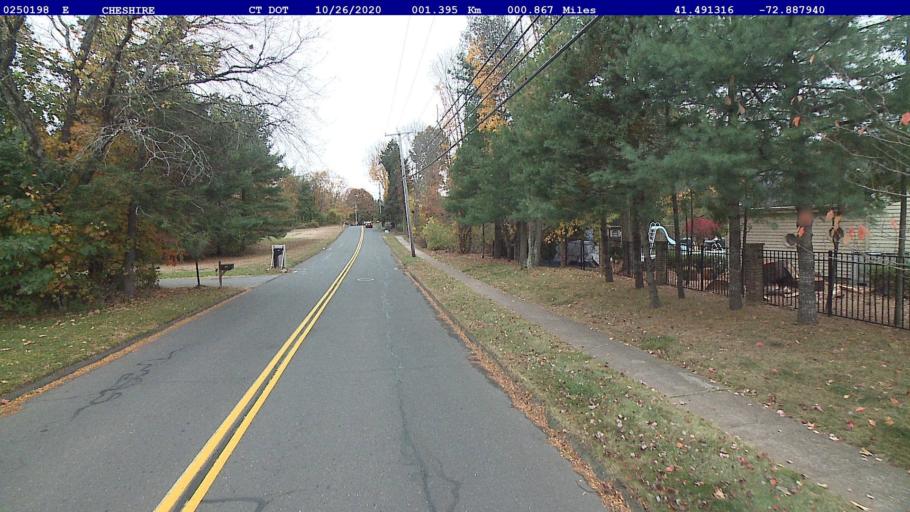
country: US
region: Connecticut
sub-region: New Haven County
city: Cheshire
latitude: 41.4913
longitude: -72.8879
